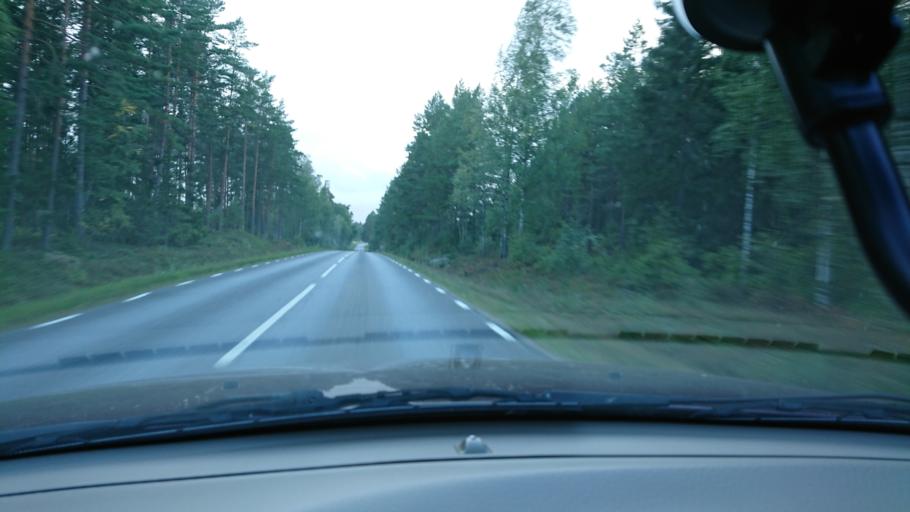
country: SE
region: Kronoberg
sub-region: Vaxjo Kommun
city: Rottne
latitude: 57.0676
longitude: 14.7346
